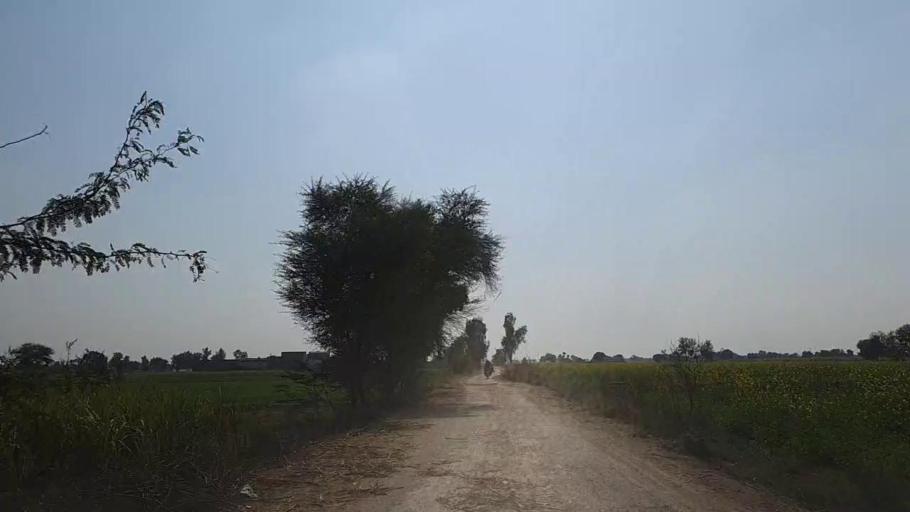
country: PK
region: Sindh
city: Daur
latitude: 26.4591
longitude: 68.2632
